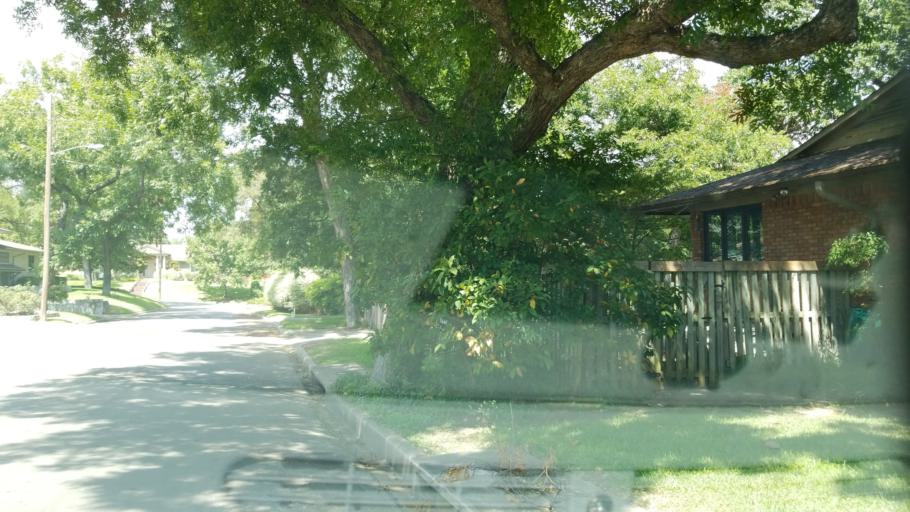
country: US
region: Texas
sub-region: Dallas County
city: Dallas
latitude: 32.7622
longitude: -96.8391
